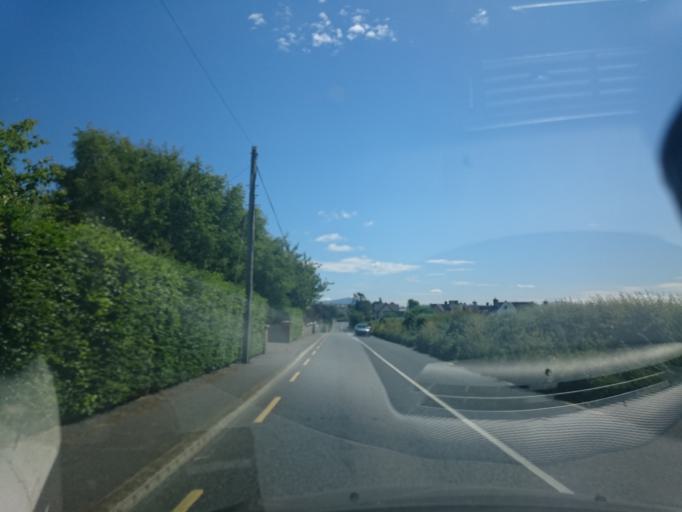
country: IE
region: Leinster
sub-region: Kilkenny
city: Thomastown
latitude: 52.6304
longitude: -7.0739
